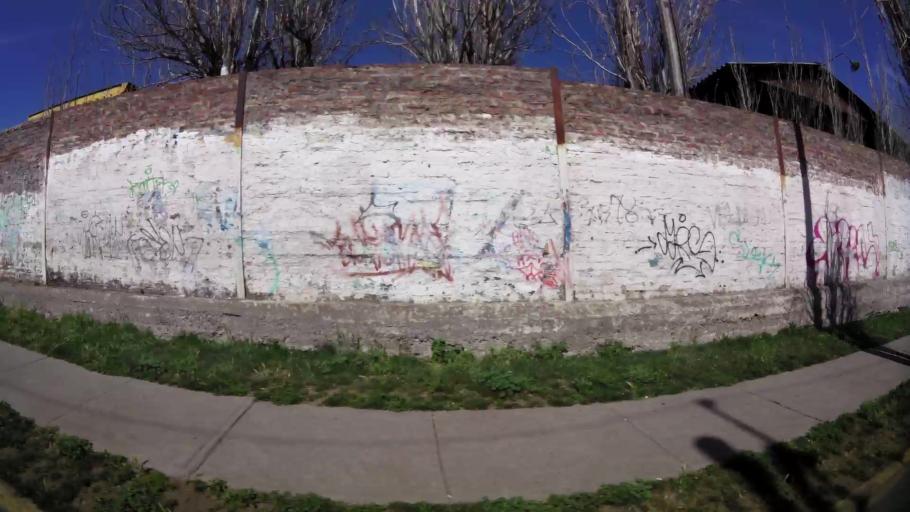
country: CL
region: Santiago Metropolitan
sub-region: Provincia de Santiago
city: Lo Prado
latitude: -33.4970
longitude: -70.7220
